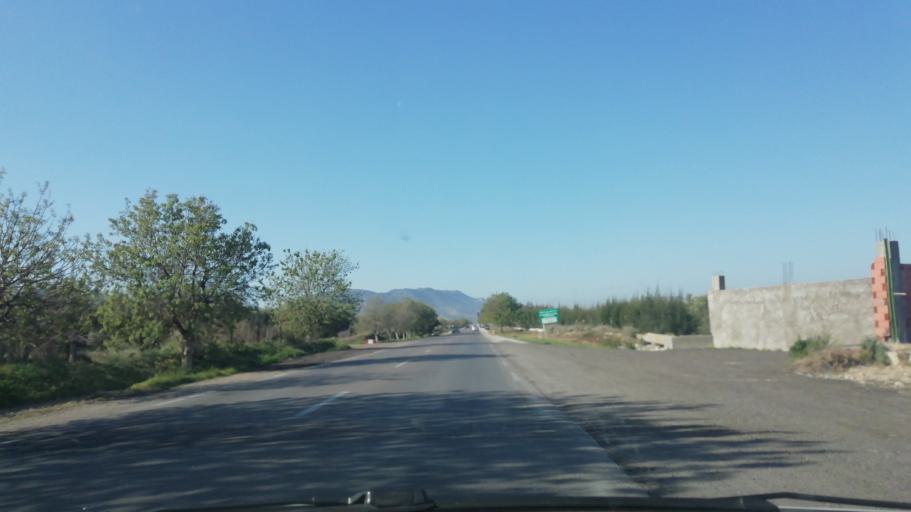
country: DZ
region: Mascara
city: Sig
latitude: 35.5470
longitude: -0.1195
